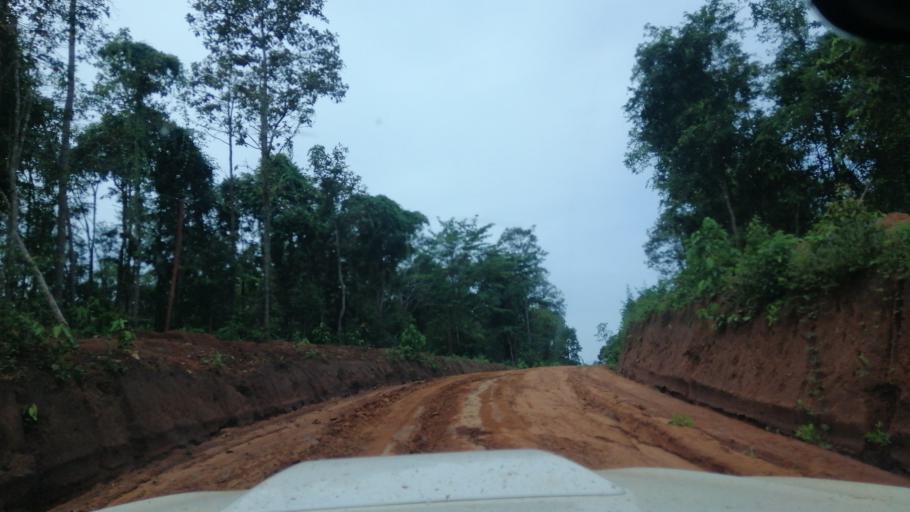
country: TH
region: Loei
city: Na Haeo
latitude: 17.5779
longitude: 101.1679
